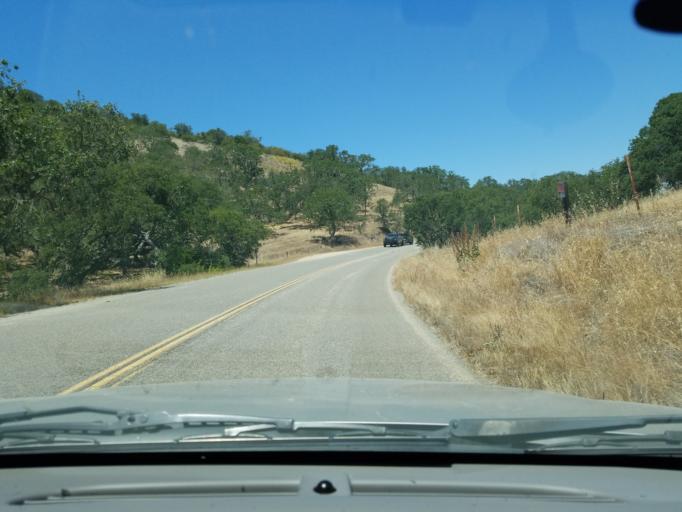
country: US
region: California
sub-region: Monterey County
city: Gonzales
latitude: 36.4026
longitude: -121.5868
